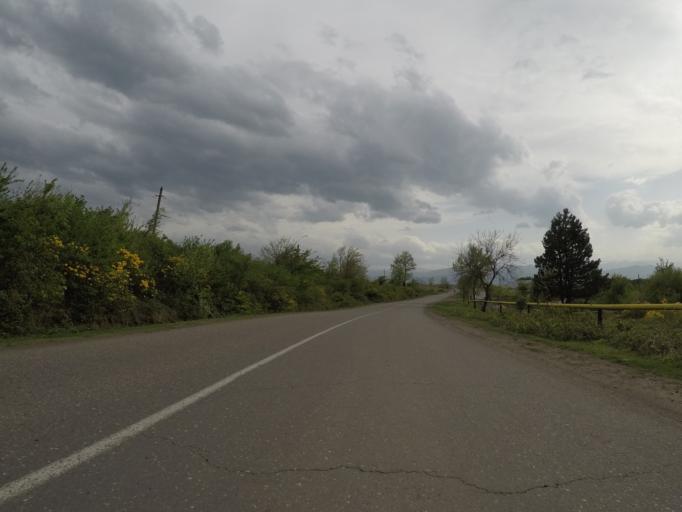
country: GE
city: Shorapani
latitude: 42.1750
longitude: 43.1314
